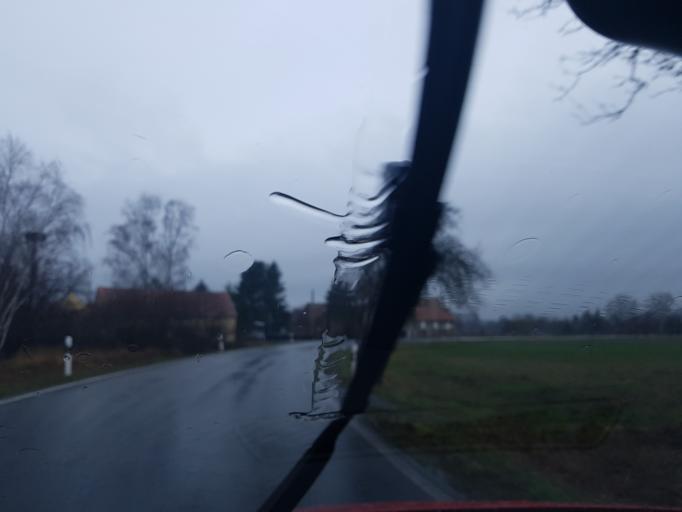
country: DE
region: Brandenburg
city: Schilda
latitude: 51.6267
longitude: 13.3150
